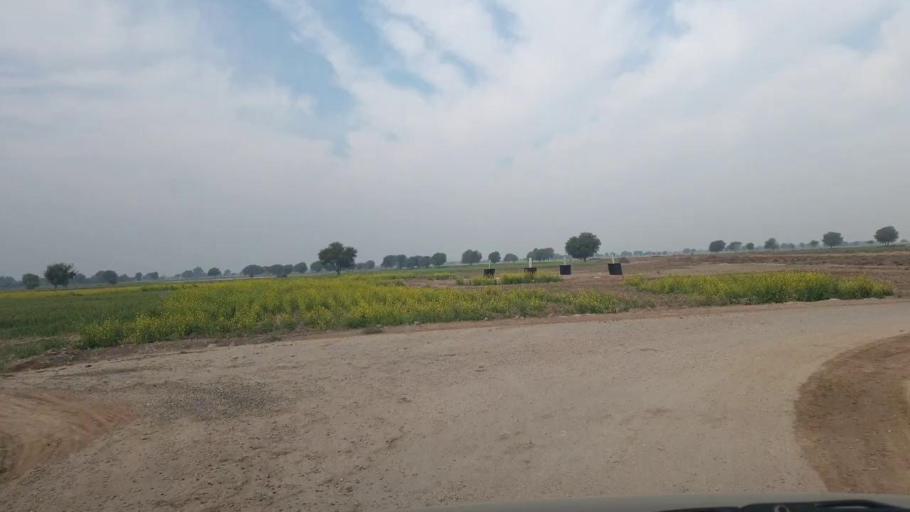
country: PK
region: Sindh
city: Shahdadpur
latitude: 25.9515
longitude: 68.6699
